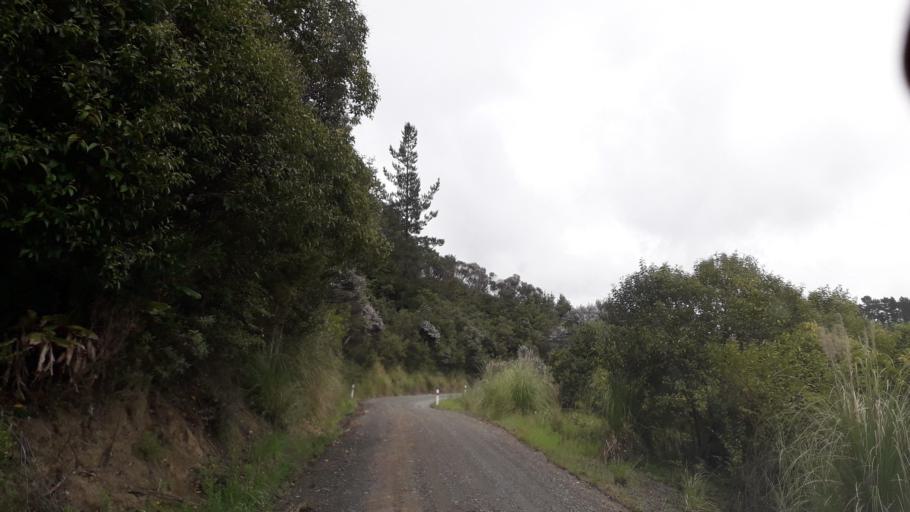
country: NZ
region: Northland
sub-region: Far North District
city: Waimate North
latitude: -35.3038
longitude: 173.5642
